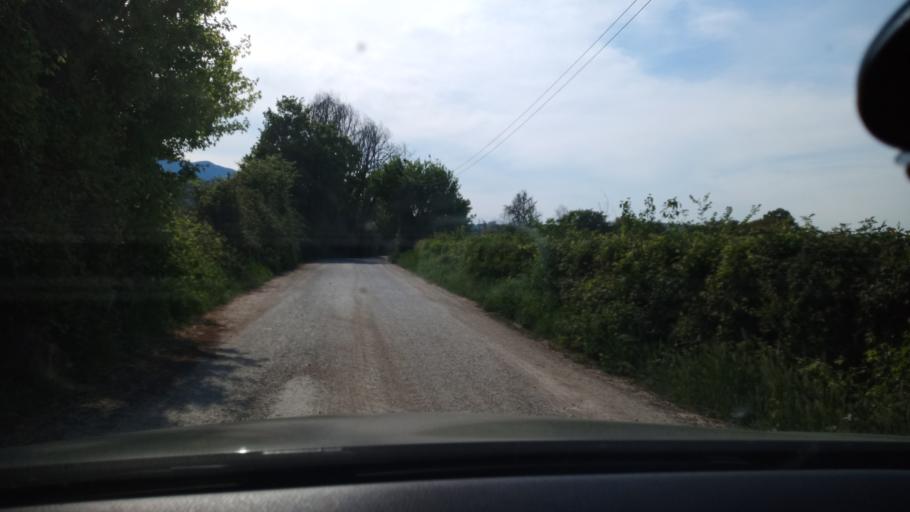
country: IT
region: Latium
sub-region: Citta metropolitana di Roma Capitale
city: Ponzano Romano
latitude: 42.2673
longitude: 12.5628
